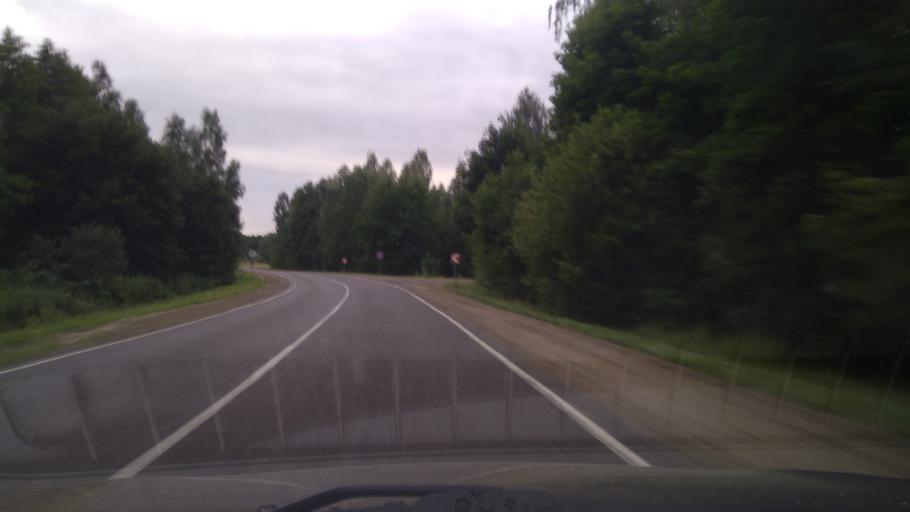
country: BY
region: Brest
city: Byaroza
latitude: 52.4128
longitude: 24.9908
